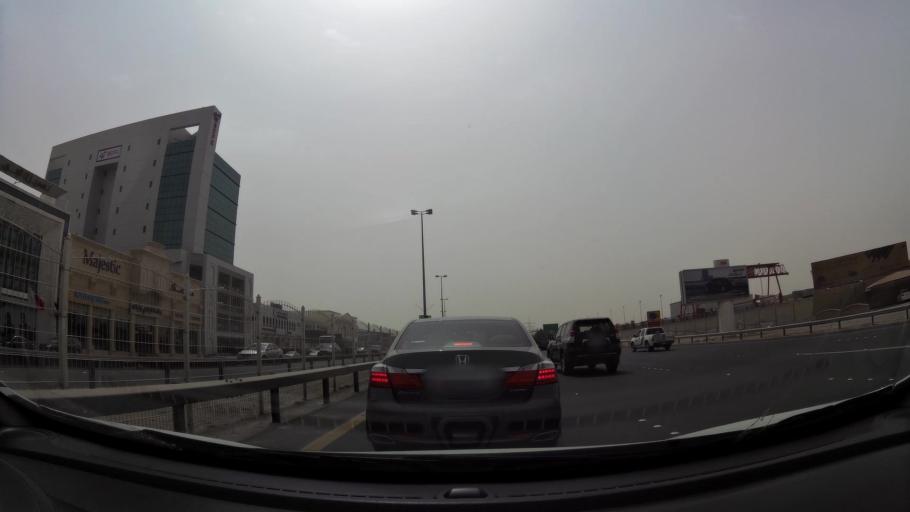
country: BH
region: Northern
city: Madinat `Isa
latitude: 26.1906
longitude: 50.5356
